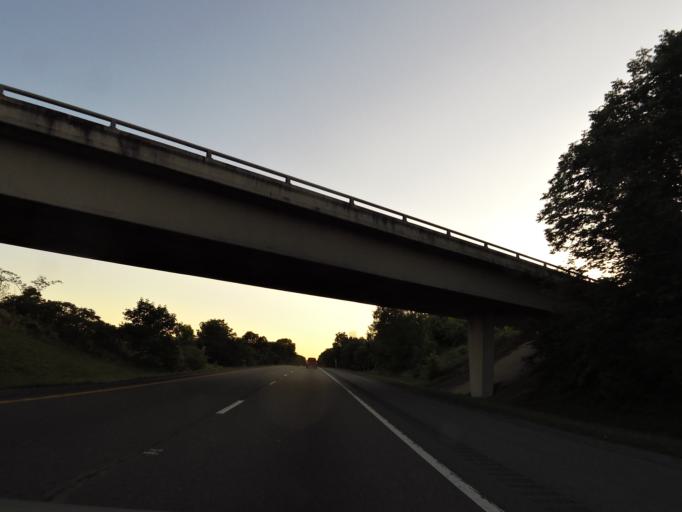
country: US
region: Tennessee
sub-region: Greene County
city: Mosheim
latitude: 36.2431
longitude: -82.9880
